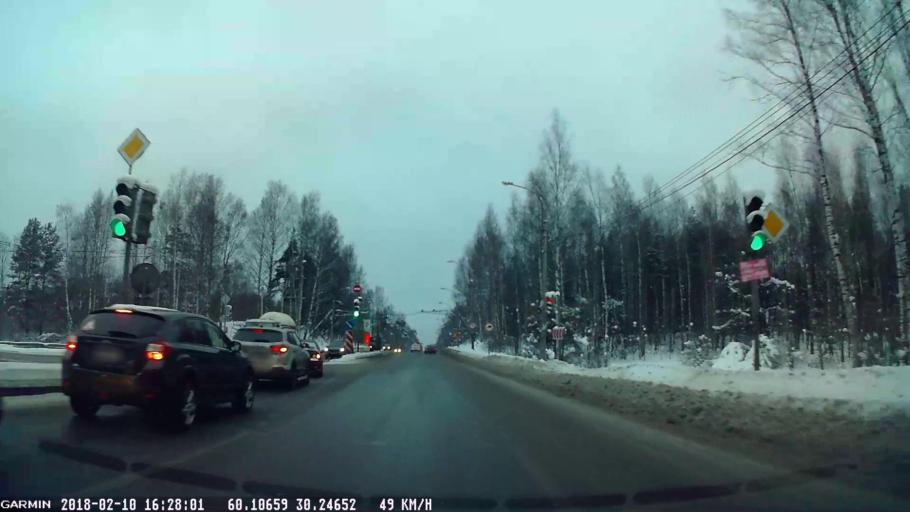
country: RU
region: St.-Petersburg
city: Pargolovo
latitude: 60.1068
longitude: 30.2463
